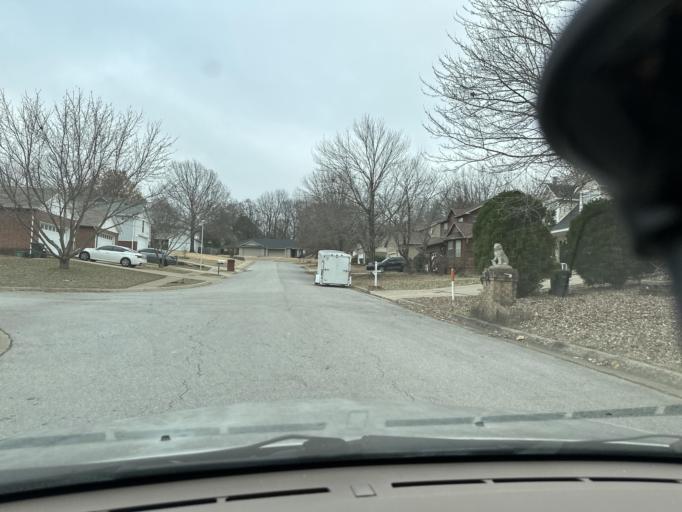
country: US
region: Arkansas
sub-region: Washington County
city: Fayetteville
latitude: 36.0841
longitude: -94.1187
